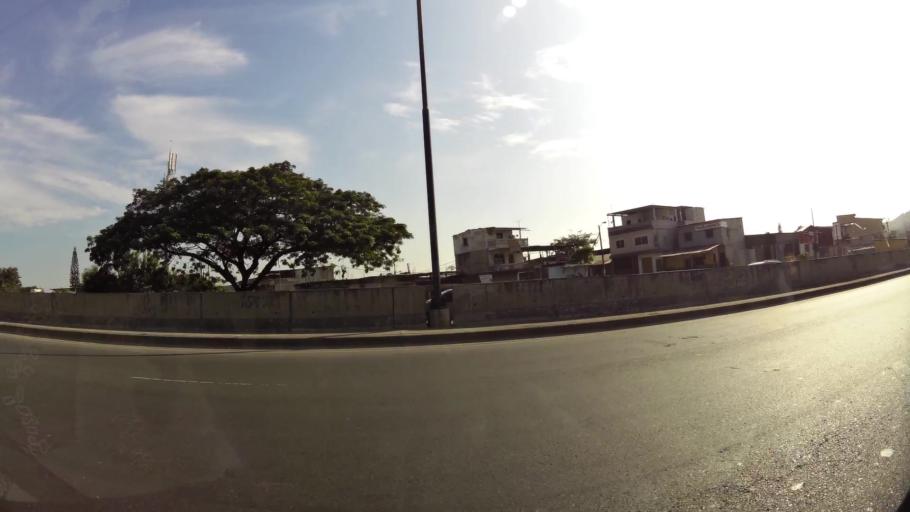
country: EC
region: Guayas
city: Eloy Alfaro
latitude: -2.0790
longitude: -79.9268
